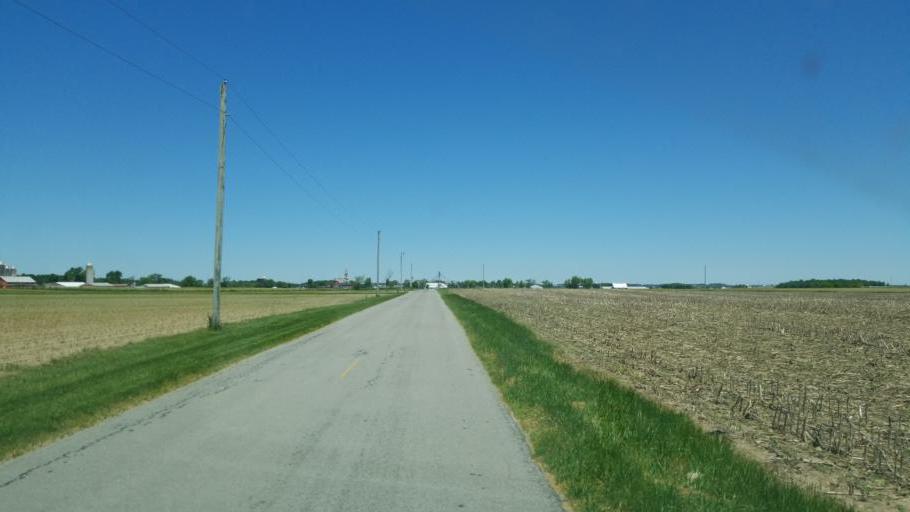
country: US
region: Ohio
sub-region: Mercer County
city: Fort Recovery
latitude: 40.3572
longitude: -84.7099
